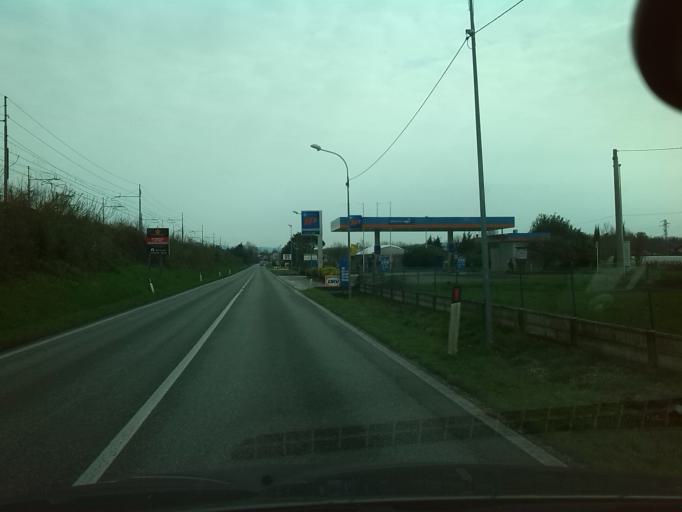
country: IT
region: Friuli Venezia Giulia
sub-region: Provincia di Gorizia
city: Cormons
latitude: 45.9507
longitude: 13.4746
